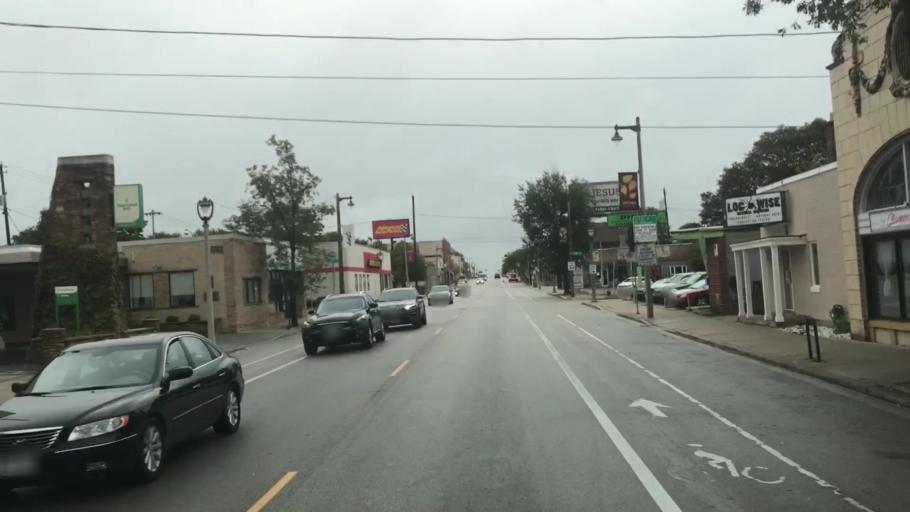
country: US
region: Wisconsin
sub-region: Milwaukee County
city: Wauwatosa
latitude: 43.0607
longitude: -87.9872
